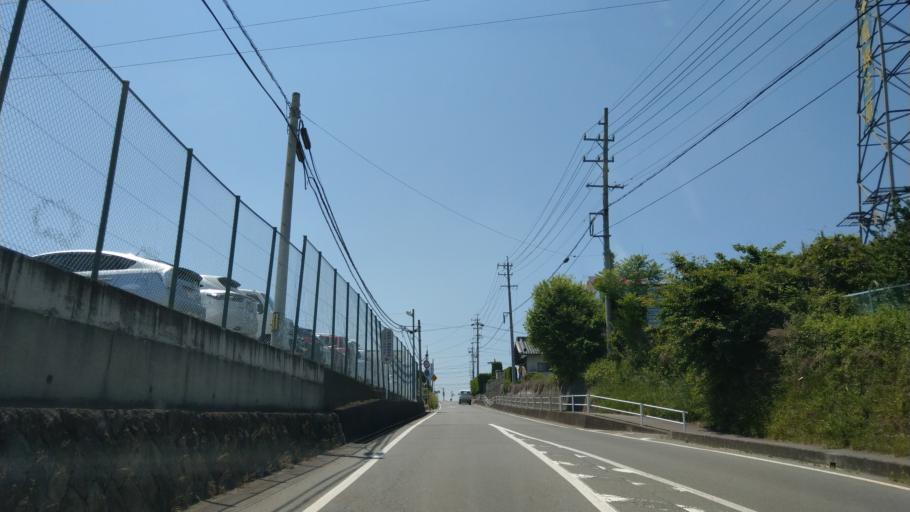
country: JP
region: Nagano
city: Komoro
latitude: 36.2928
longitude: 138.4399
